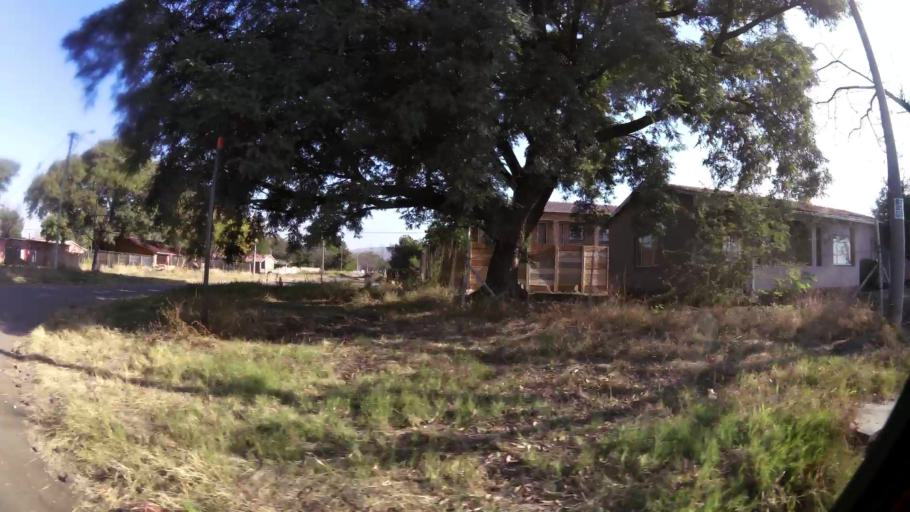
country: ZA
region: North-West
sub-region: Bojanala Platinum District Municipality
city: Rustenburg
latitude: -25.6470
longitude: 27.2342
